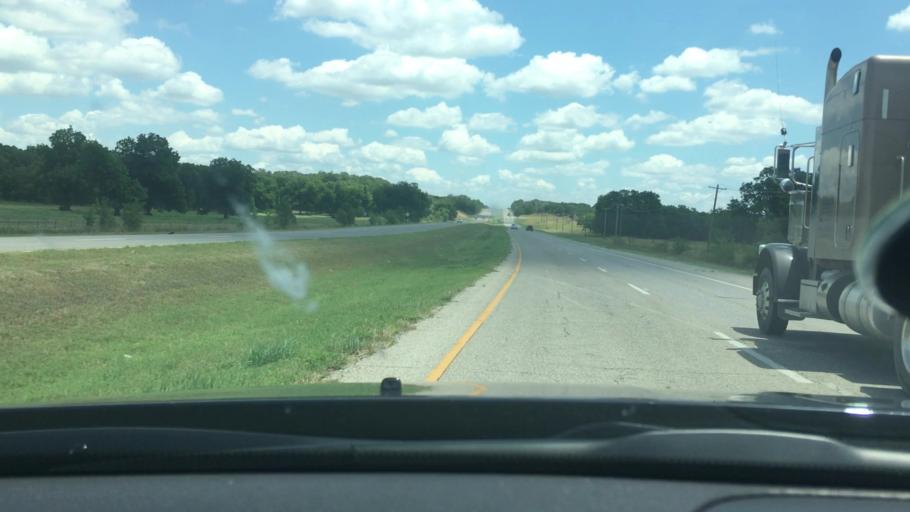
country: US
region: Oklahoma
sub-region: Carter County
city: Wilson
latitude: 34.1728
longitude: -97.3605
